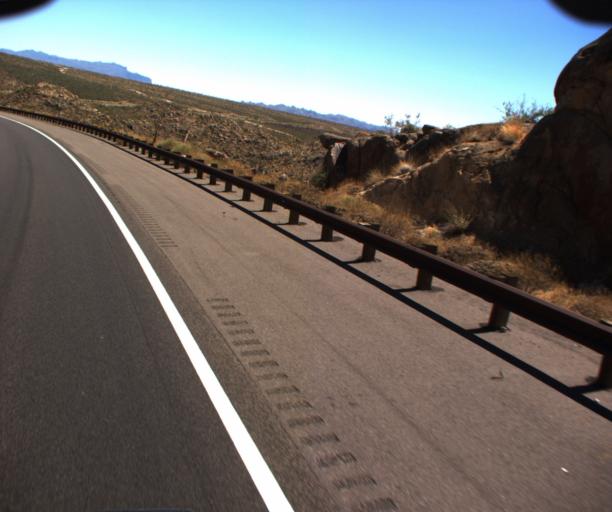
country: US
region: Arizona
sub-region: Maricopa County
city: Rio Verde
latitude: 33.6923
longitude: -111.5029
